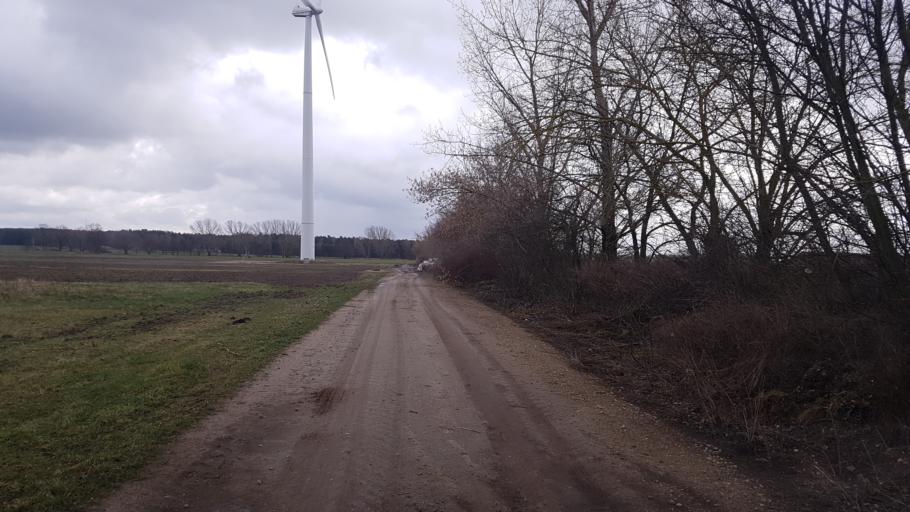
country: DE
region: Brandenburg
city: Bronkow
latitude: 51.6438
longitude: 13.8750
